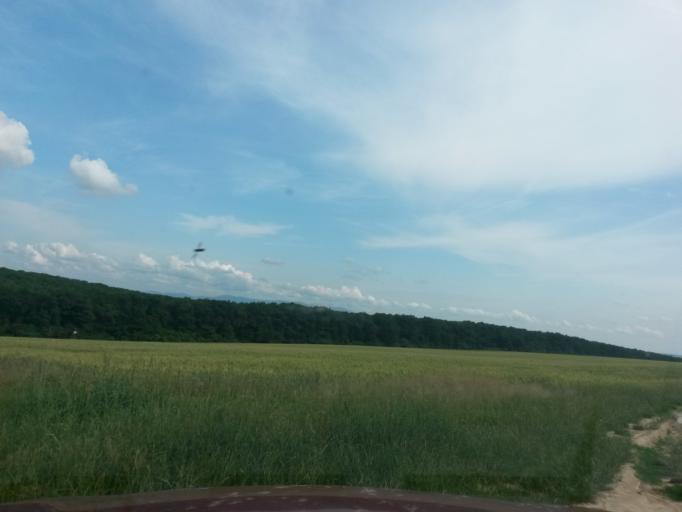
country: SK
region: Kosicky
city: Moldava nad Bodvou
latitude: 48.6335
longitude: 21.1060
